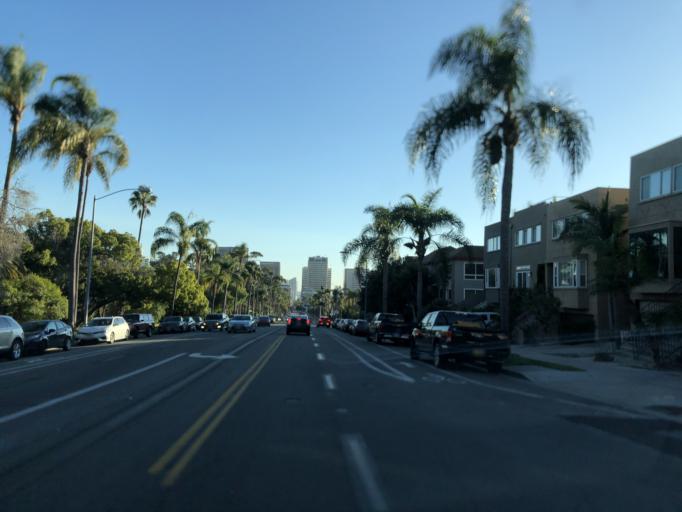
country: US
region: California
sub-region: San Diego County
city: San Diego
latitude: 32.7283
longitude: -117.1594
